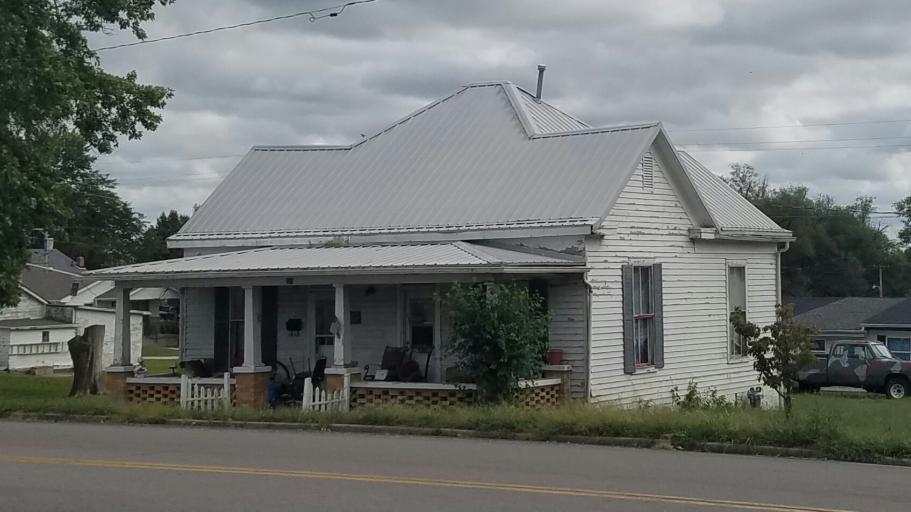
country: US
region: Missouri
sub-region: Moniteau County
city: California
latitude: 38.6277
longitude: -92.5659
